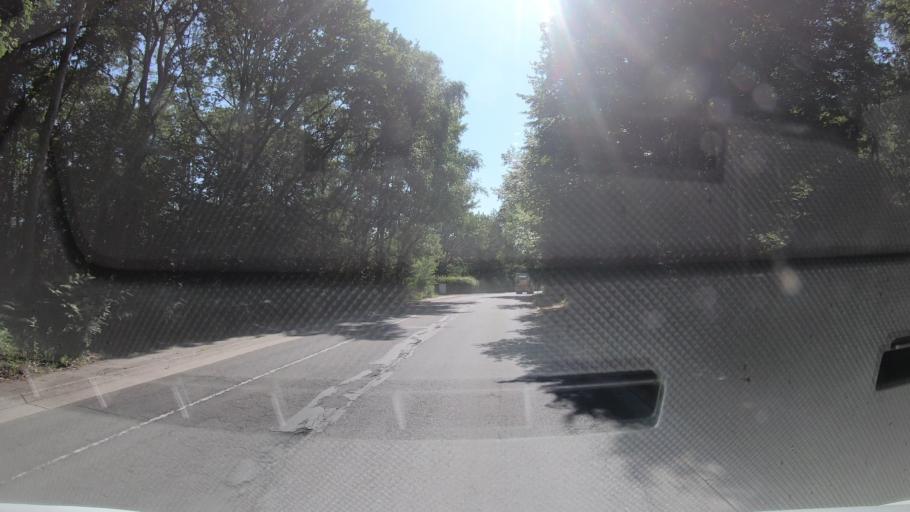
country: BE
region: Wallonia
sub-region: Province de Liege
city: Liege
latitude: 50.5980
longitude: 5.5739
